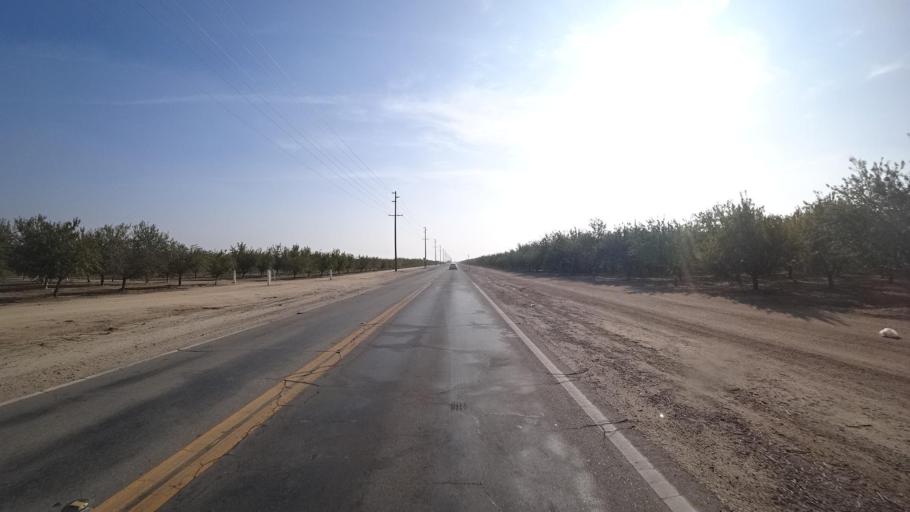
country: US
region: California
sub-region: Kern County
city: Delano
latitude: 35.7584
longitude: -119.2233
